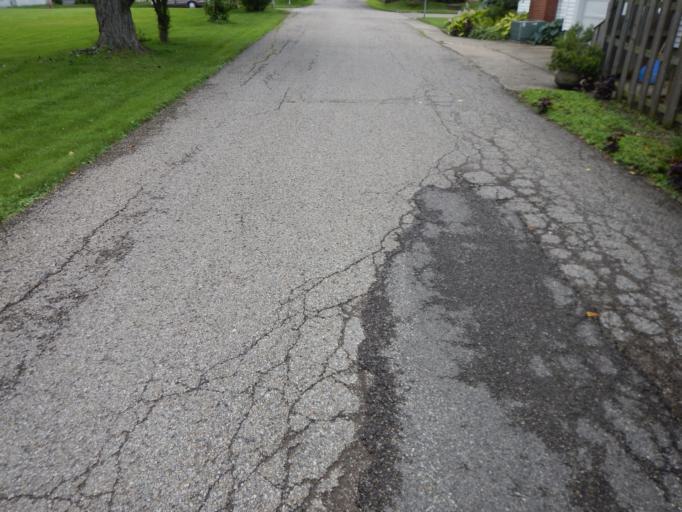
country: US
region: Ohio
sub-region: Muskingum County
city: North Zanesville
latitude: 39.9657
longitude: -82.0117
